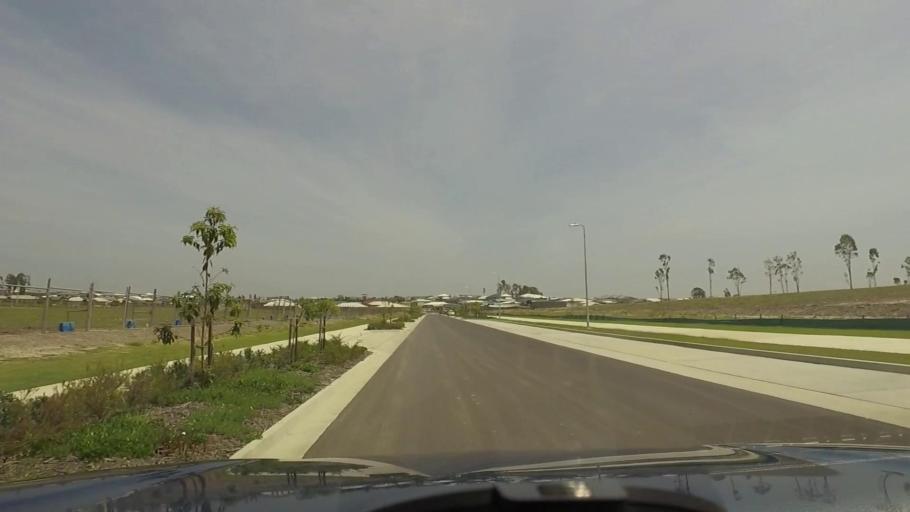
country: AU
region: Queensland
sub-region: Logan
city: Chambers Flat
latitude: -27.8092
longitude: 153.1201
